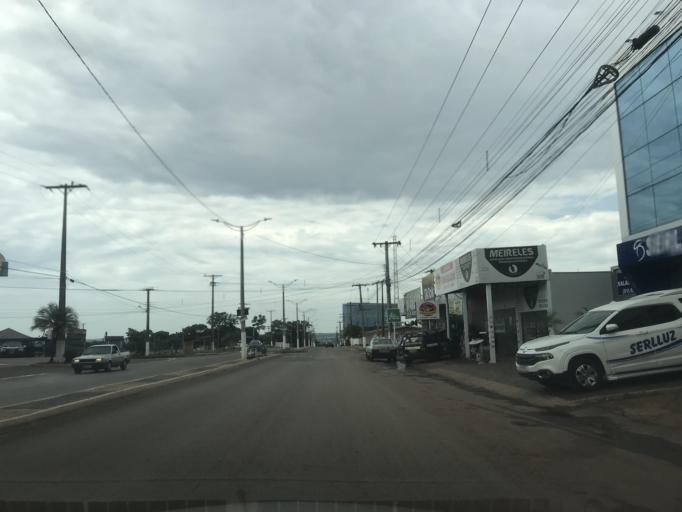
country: BR
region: Goias
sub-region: Luziania
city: Luziania
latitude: -16.2379
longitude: -47.9425
